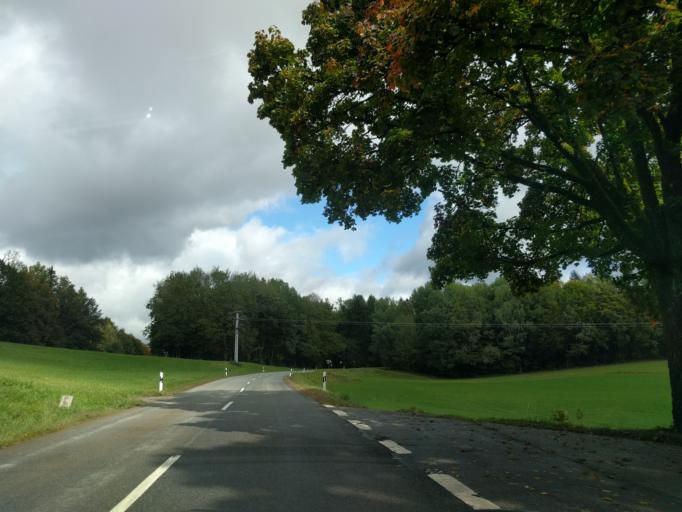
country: DE
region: Bavaria
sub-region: Lower Bavaria
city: Deggendorf
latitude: 48.8370
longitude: 13.0056
